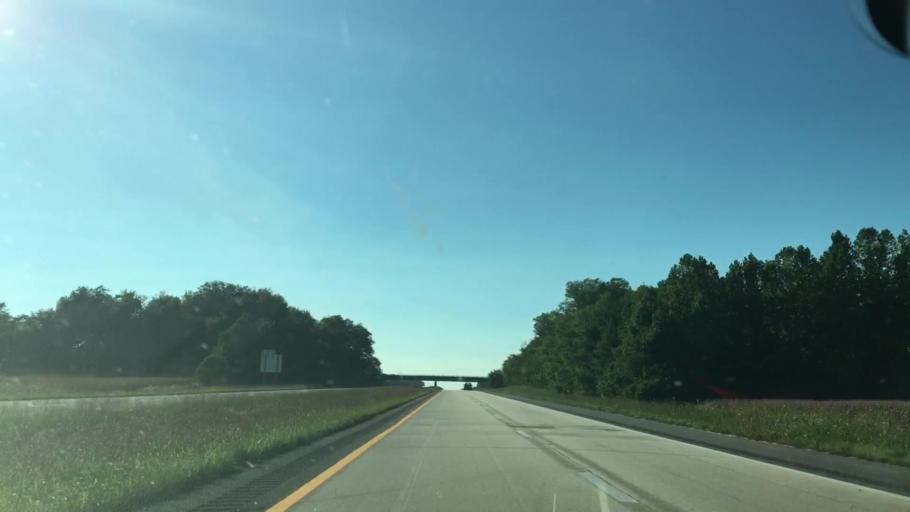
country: US
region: Kentucky
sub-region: Henderson County
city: Henderson
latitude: 37.7928
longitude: -87.4913
